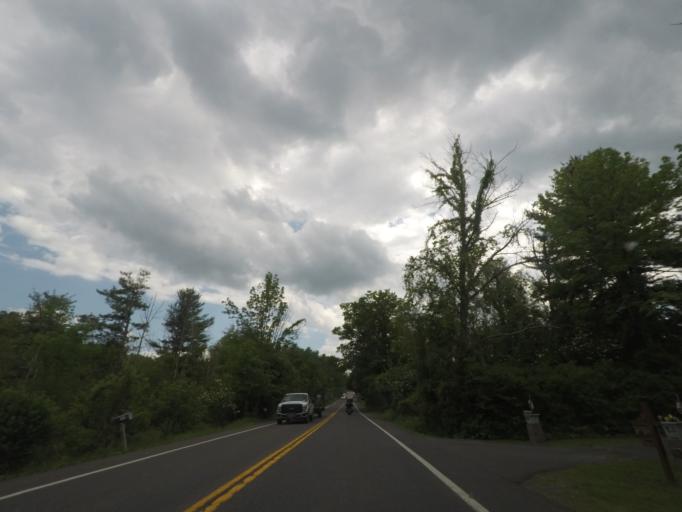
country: US
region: New York
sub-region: Dutchess County
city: Pine Plains
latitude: 42.0791
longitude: -73.6724
